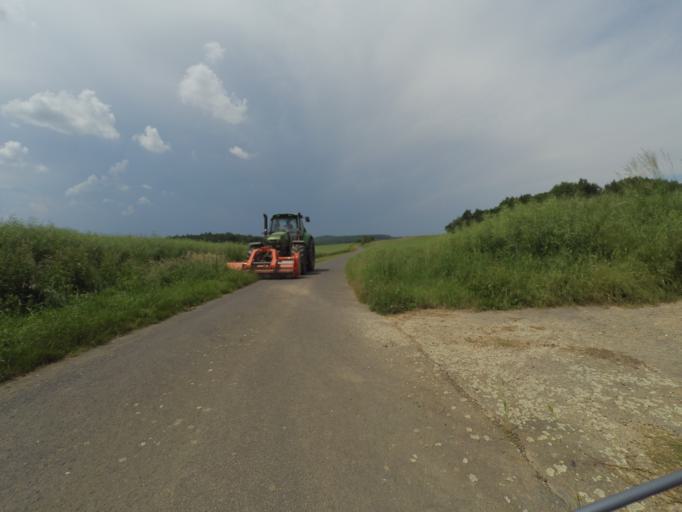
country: DE
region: Rheinland-Pfalz
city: Morshausen
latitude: 50.1979
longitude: 7.4389
